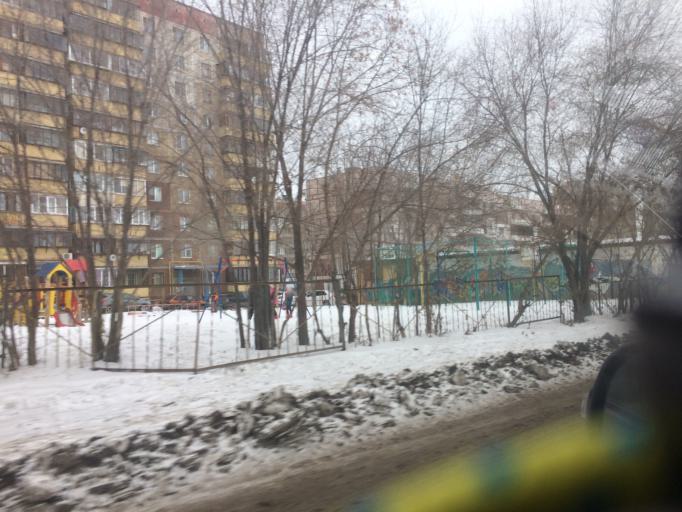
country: RU
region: Chelyabinsk
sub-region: Gorod Magnitogorsk
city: Magnitogorsk
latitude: 53.3603
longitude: 58.9916
